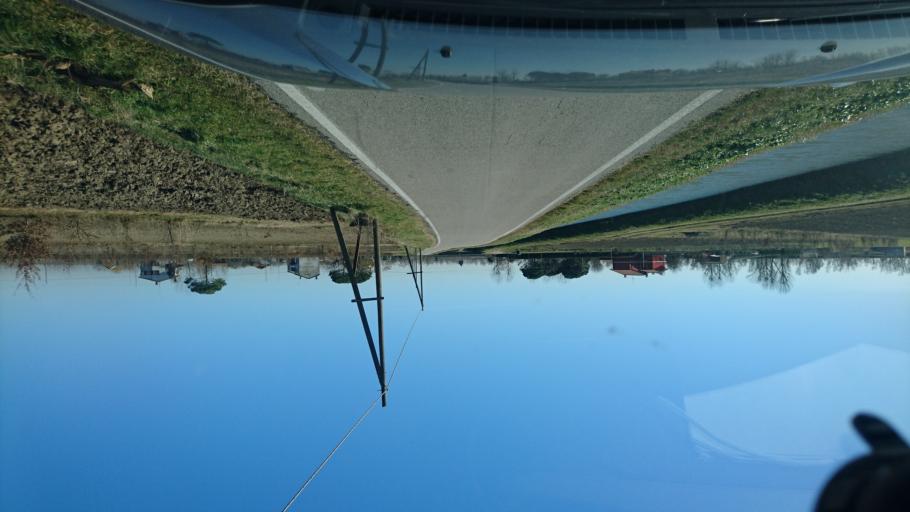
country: IT
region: Emilia-Romagna
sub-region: Provincia di Ferrara
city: Mesola
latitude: 44.9319
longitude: 12.2087
